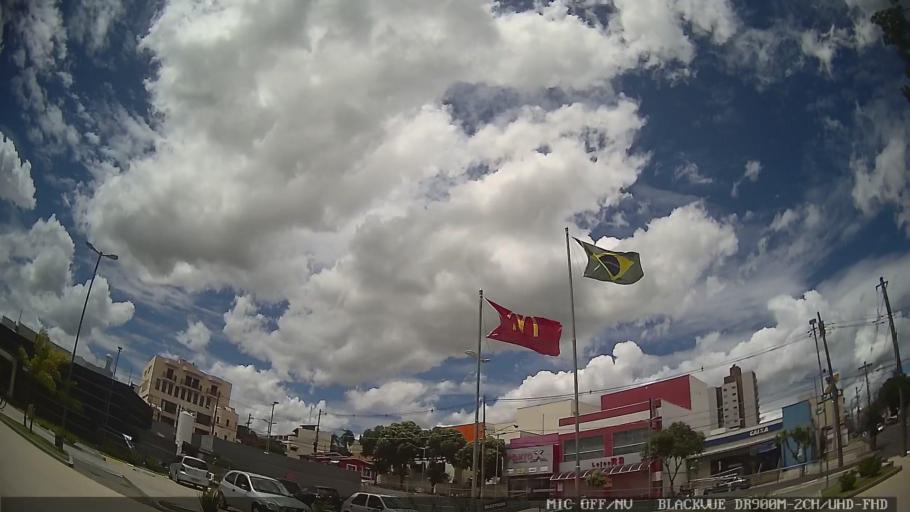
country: BR
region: Sao Paulo
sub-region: Jaguariuna
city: Jaguariuna
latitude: -22.7080
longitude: -46.9872
